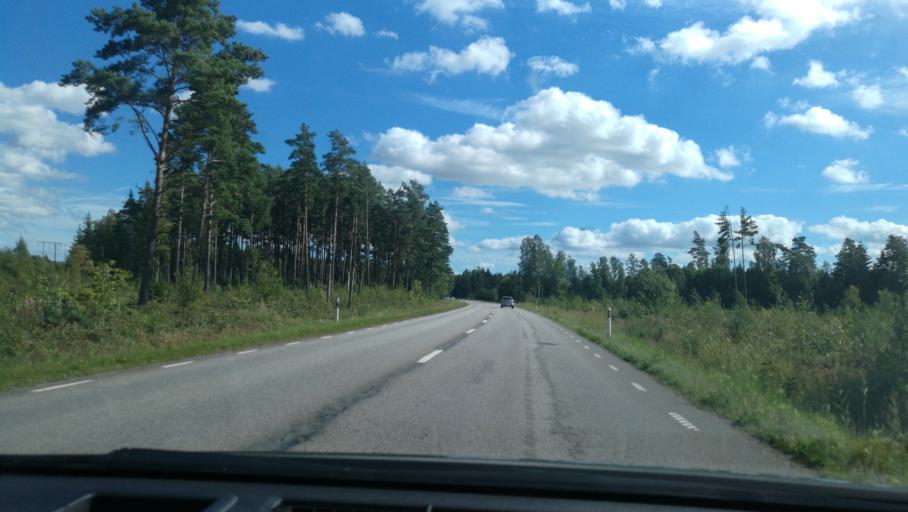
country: SE
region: Vaestra Goetaland
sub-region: Lidkopings Kommun
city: Vinninga
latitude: 58.4915
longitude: 13.2730
